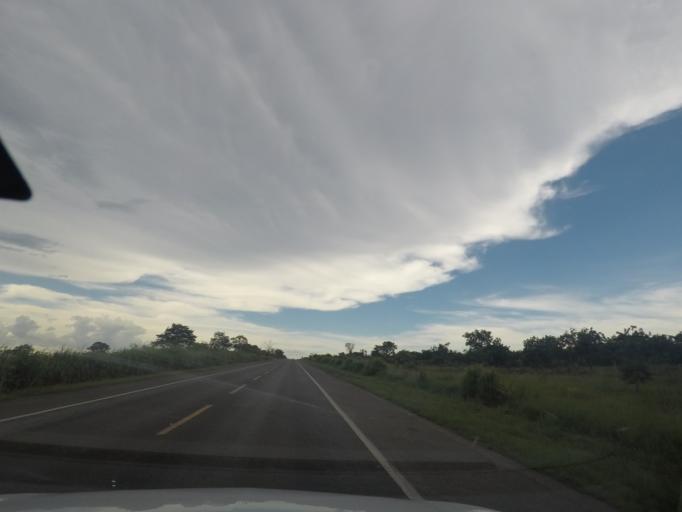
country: BR
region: Minas Gerais
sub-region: Prata
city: Prata
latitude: -19.5883
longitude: -48.8288
